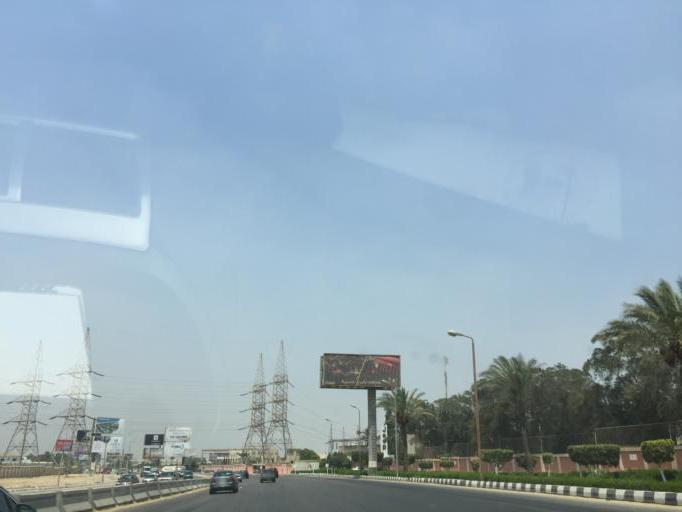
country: EG
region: Muhafazat al Qalyubiyah
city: Al Khankah
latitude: 30.0814
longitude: 31.4128
